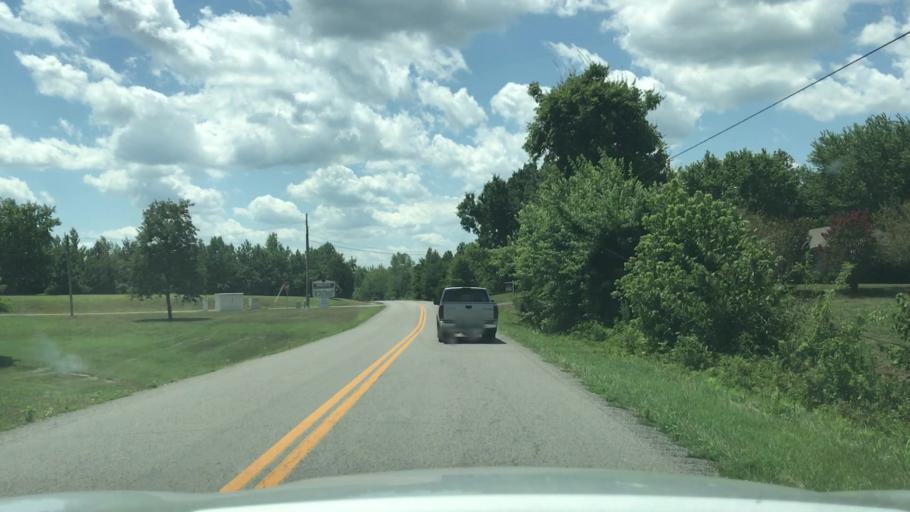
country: US
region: Kentucky
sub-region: Muhlenberg County
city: Greenville
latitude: 37.1787
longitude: -87.2376
